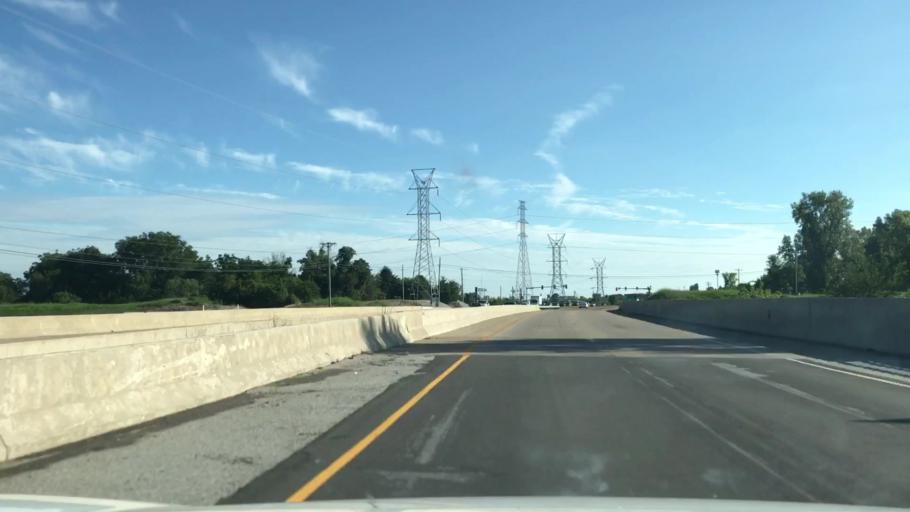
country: US
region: Illinois
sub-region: Madison County
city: Hartford
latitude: 38.8062
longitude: -90.0990
